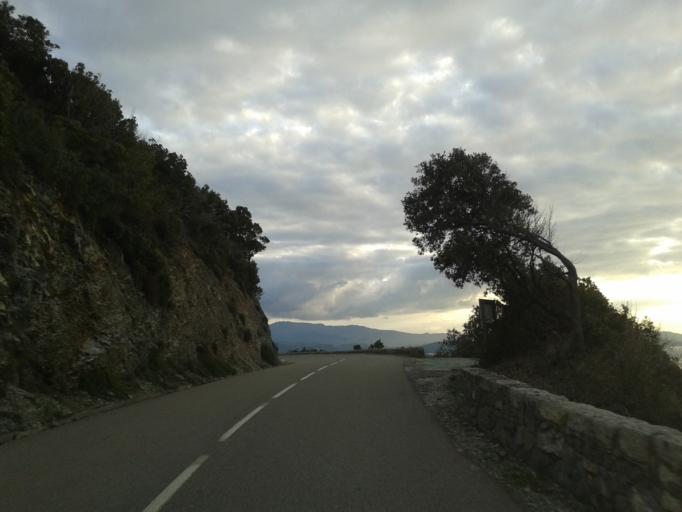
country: FR
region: Corsica
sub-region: Departement de la Haute-Corse
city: Saint-Florent
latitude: 42.7592
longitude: 9.3398
